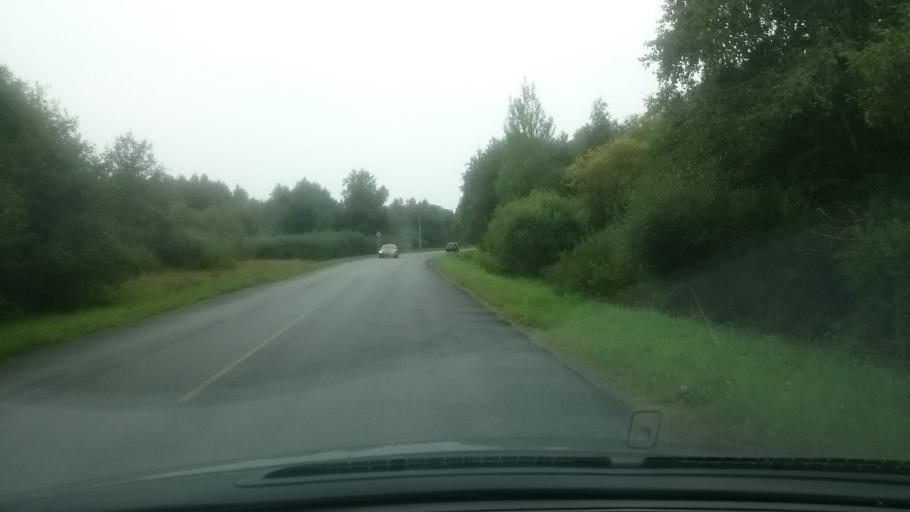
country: EE
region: Harju
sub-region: Raasiku vald
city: Raasiku
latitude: 59.4497
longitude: 25.1992
